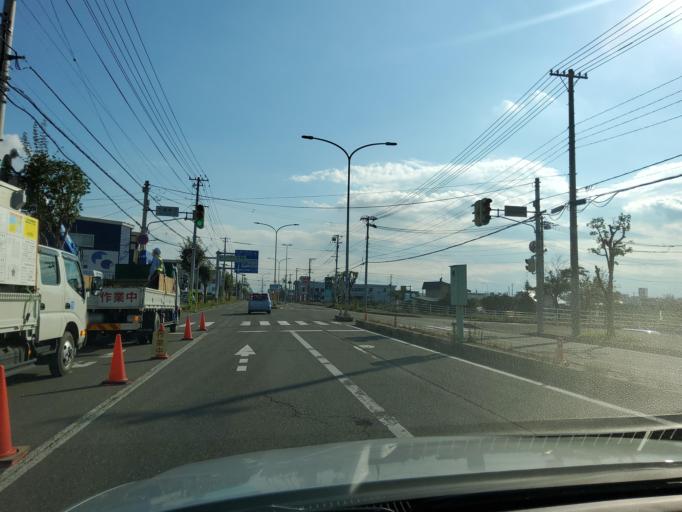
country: JP
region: Hokkaido
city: Obihiro
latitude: 42.8934
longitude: 143.2069
